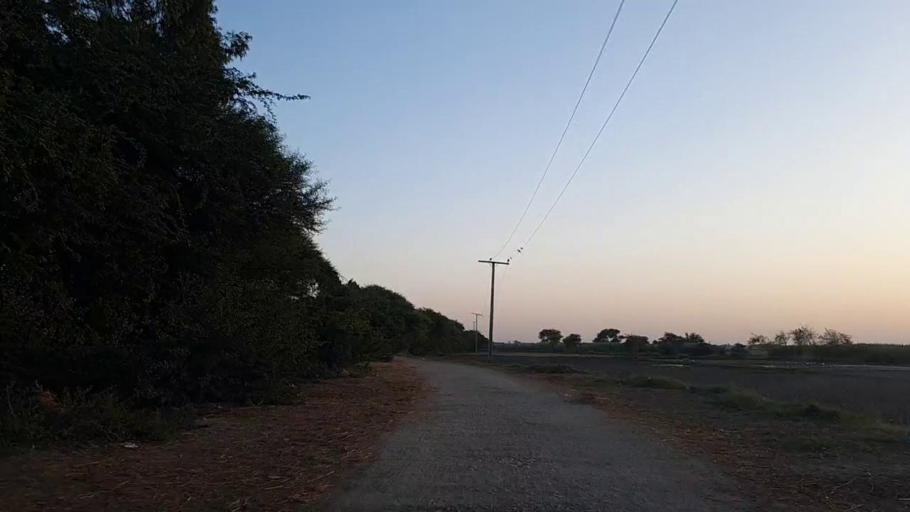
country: PK
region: Sindh
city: Mirpur Batoro
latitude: 24.6429
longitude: 68.1896
